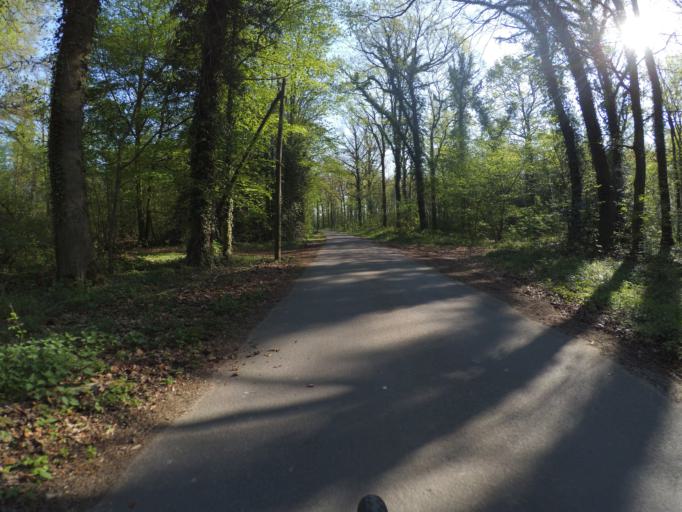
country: DE
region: North Rhine-Westphalia
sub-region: Regierungsbezirk Munster
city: Senden
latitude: 51.8541
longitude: 7.5139
